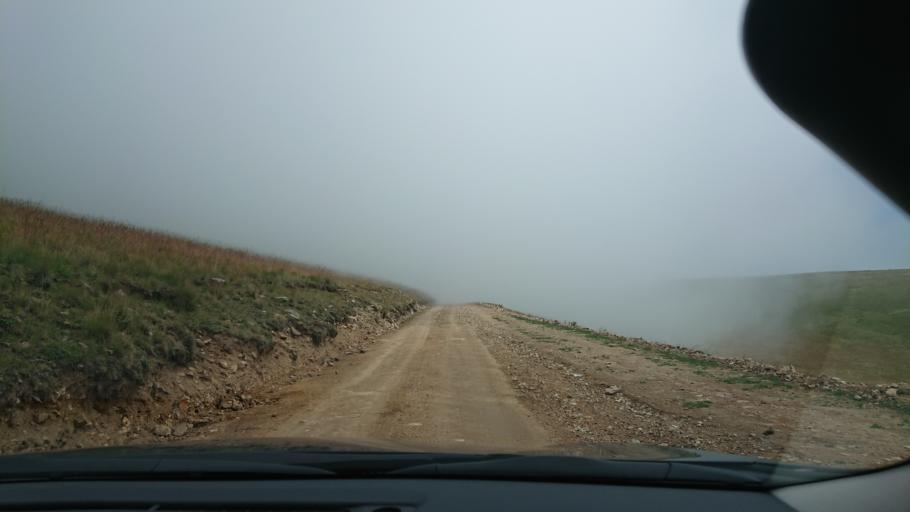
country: TR
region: Gumushane
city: Kurtun
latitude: 40.6340
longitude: 38.9937
